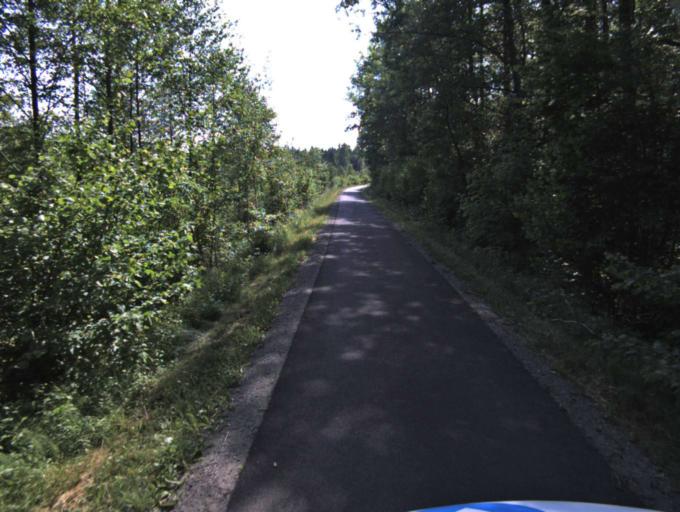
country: SE
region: Skane
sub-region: Kristianstads Kommun
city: Tollarp
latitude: 56.1986
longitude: 14.2810
